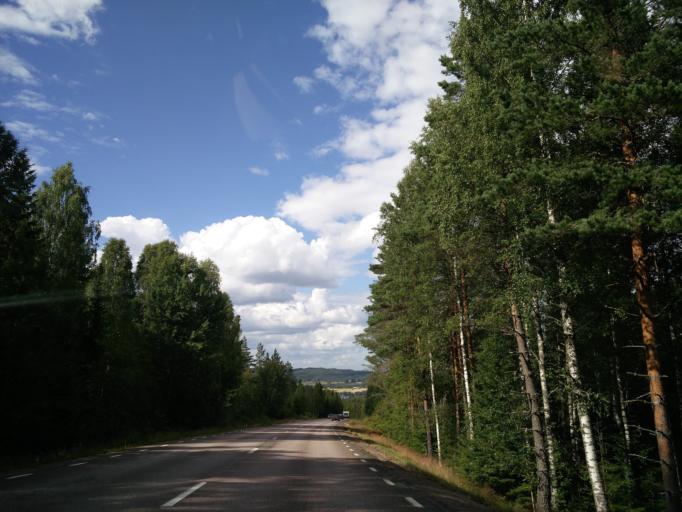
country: SE
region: Vaermland
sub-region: Sunne Kommun
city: Sunne
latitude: 59.7032
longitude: 13.1062
